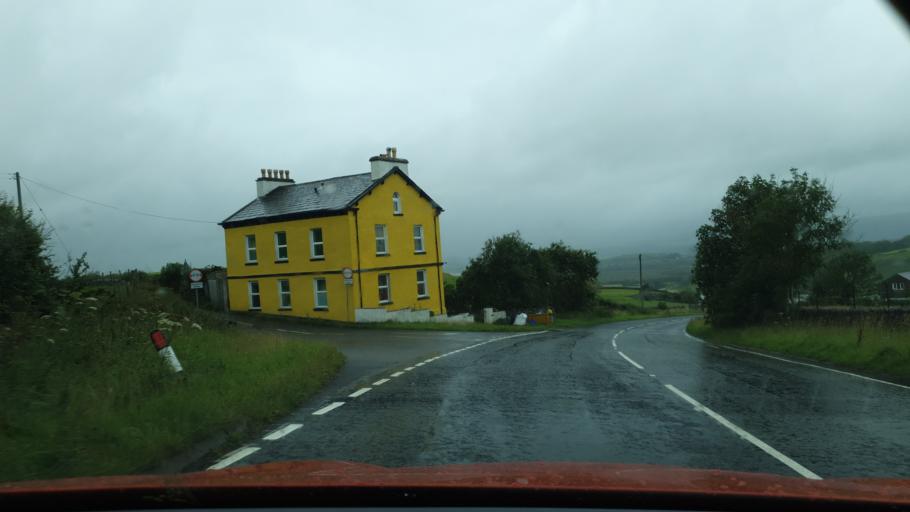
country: GB
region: England
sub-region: Cumbria
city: Ulverston
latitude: 54.2532
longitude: -3.1580
